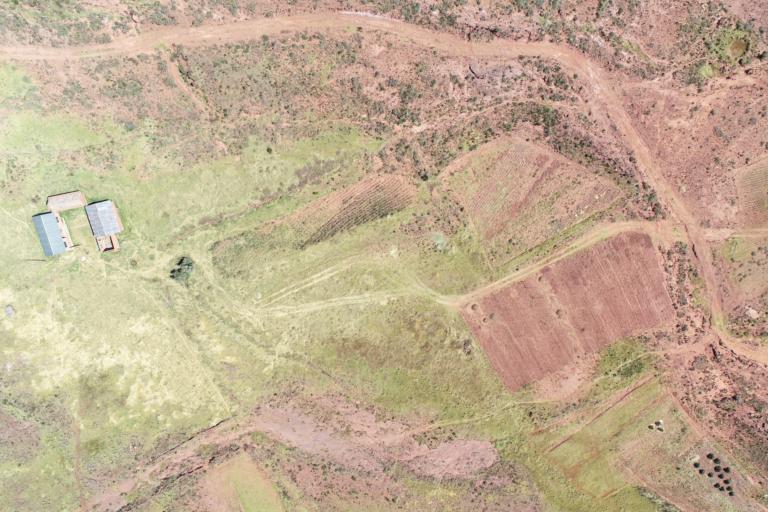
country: BO
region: La Paz
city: Tiahuanaco
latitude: -16.6051
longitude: -68.7687
